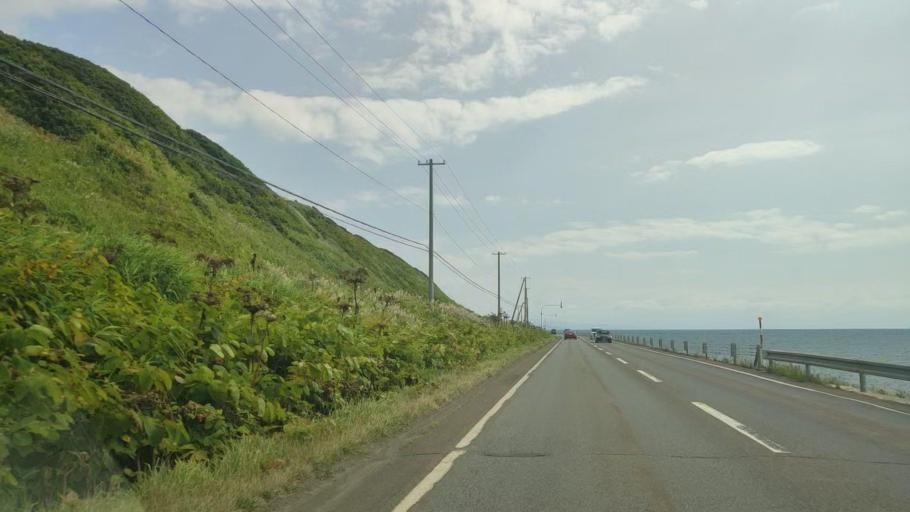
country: JP
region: Hokkaido
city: Rumoi
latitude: 44.0996
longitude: 141.6604
